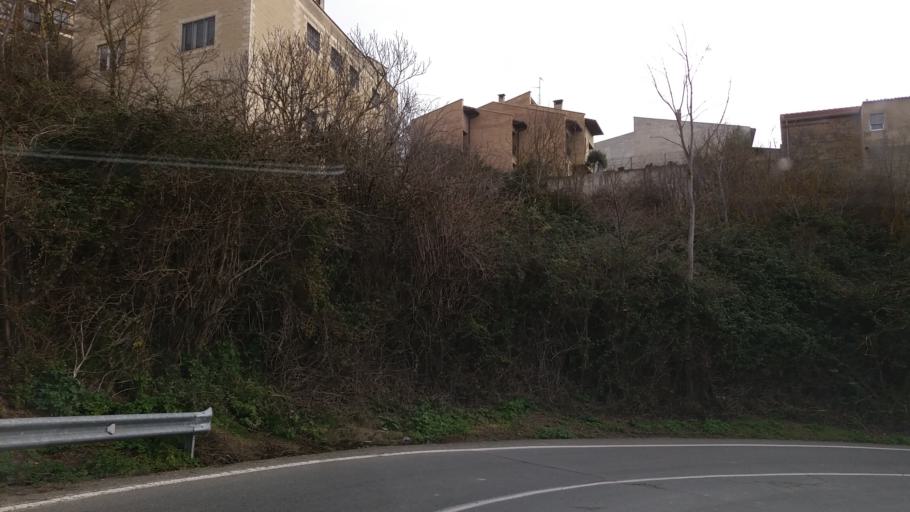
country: ES
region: La Rioja
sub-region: Provincia de La Rioja
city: San Vicente de la Sonsierra
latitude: 42.5638
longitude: -2.7615
